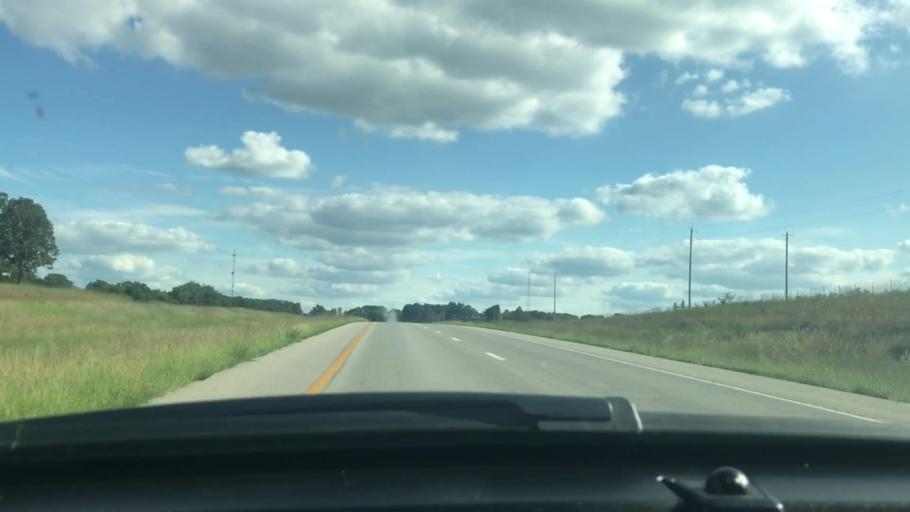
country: US
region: Missouri
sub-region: Howell County
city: West Plains
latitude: 36.8279
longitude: -91.9140
